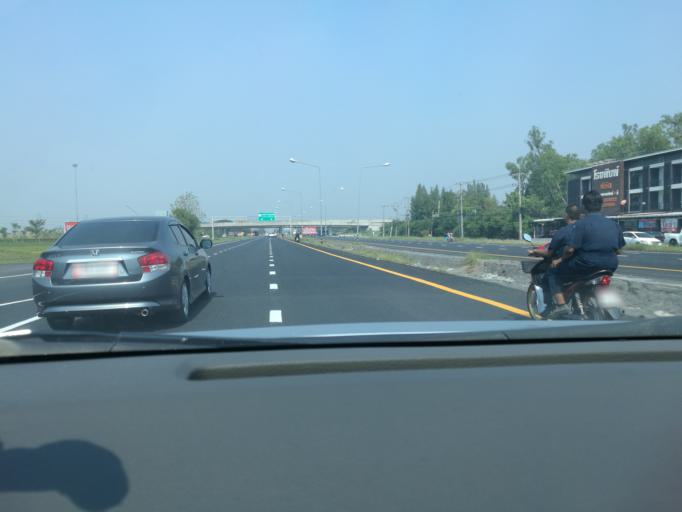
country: TH
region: Sara Buri
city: Saraburi
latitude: 14.5594
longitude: 100.9055
